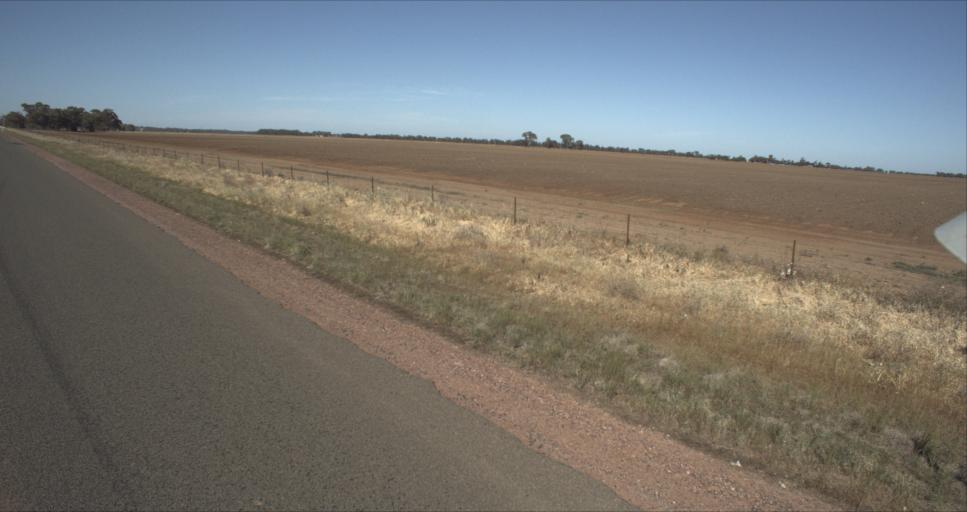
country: AU
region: New South Wales
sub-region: Leeton
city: Leeton
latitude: -34.5724
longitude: 146.2632
